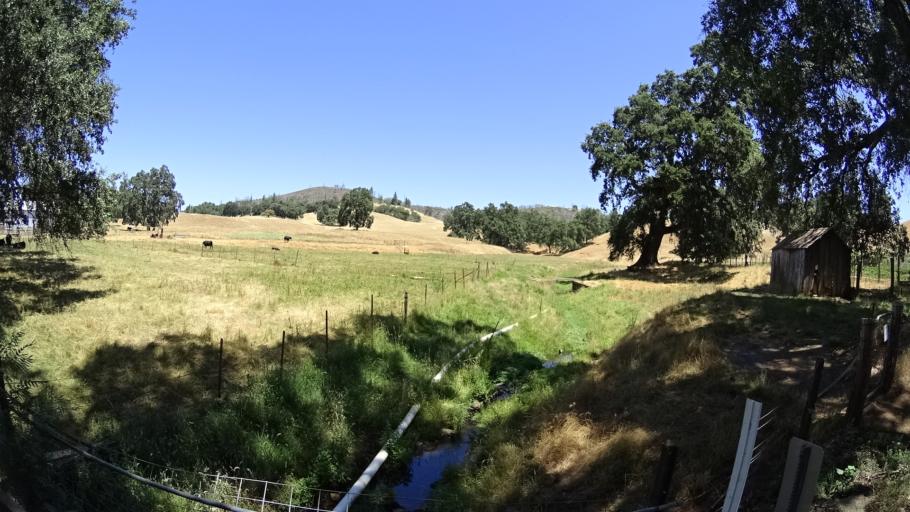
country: US
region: California
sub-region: Calaveras County
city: Mountain Ranch
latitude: 38.2368
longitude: -120.5561
